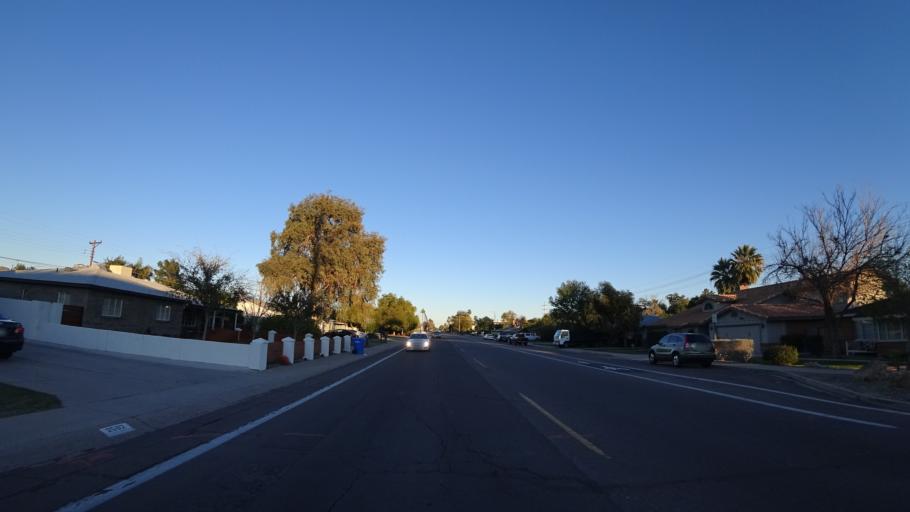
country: US
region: Arizona
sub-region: Maricopa County
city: Phoenix
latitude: 33.5022
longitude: -112.0279
